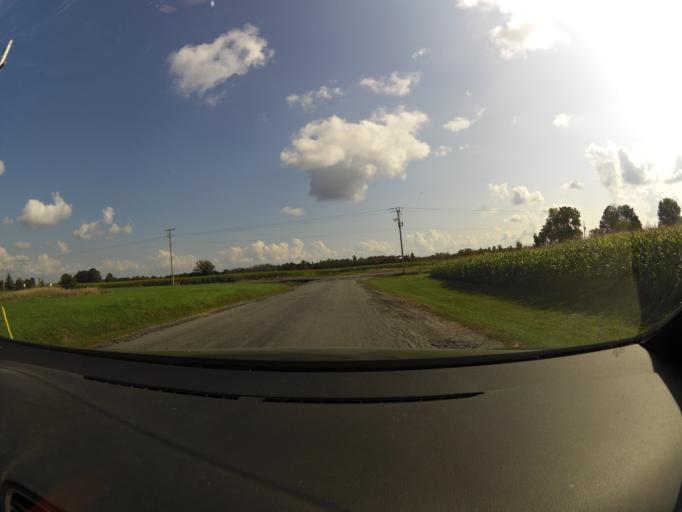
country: CA
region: Ontario
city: Carleton Place
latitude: 45.3502
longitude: -76.1348
